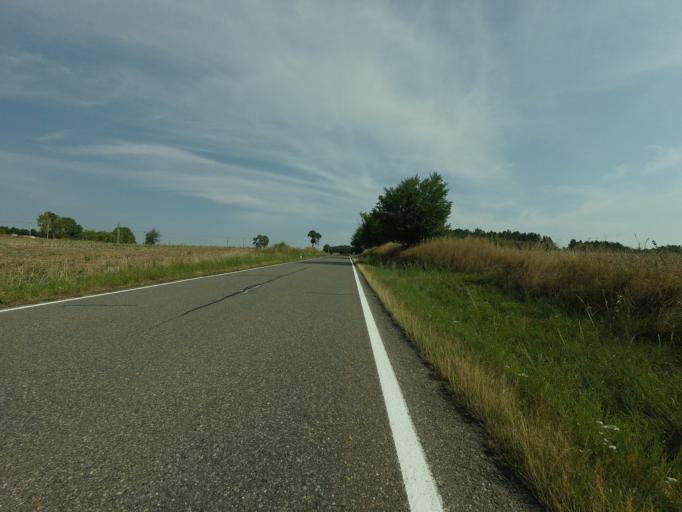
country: CZ
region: Jihocesky
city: Milevsko
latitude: 49.5000
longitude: 14.3627
